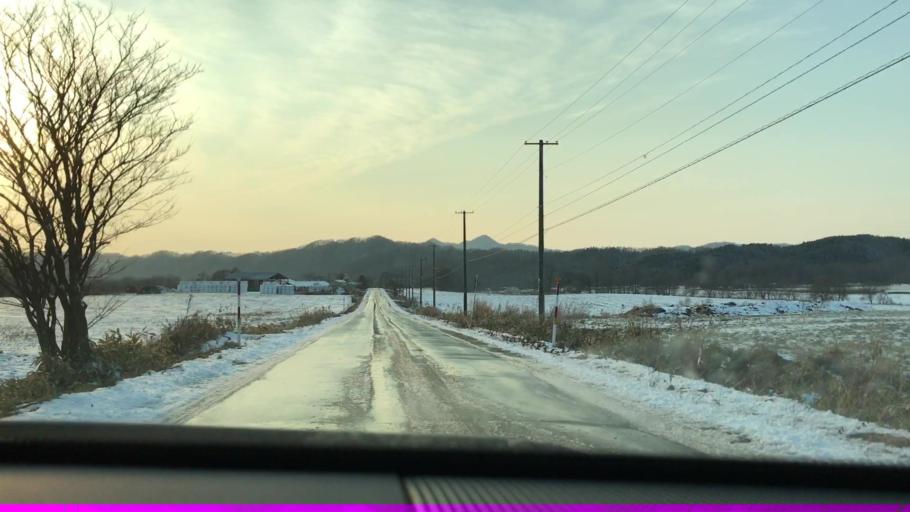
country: JP
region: Hokkaido
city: Shizunai-furukawacho
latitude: 42.5263
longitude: 142.3913
